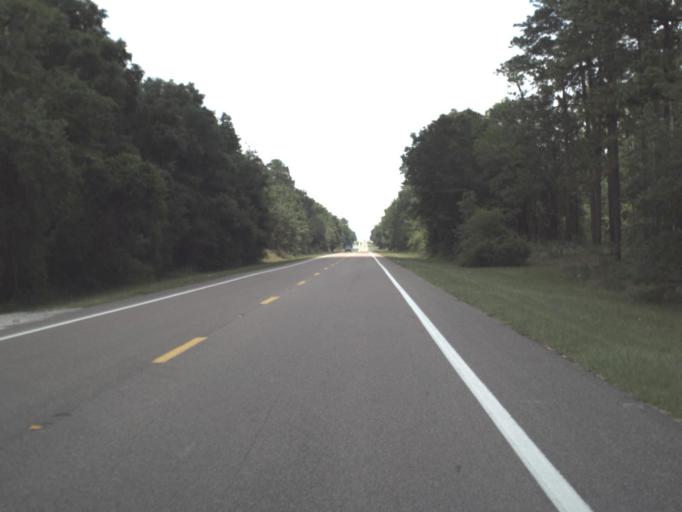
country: US
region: Florida
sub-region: Putnam County
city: Crescent City
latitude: 29.4162
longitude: -81.7371
